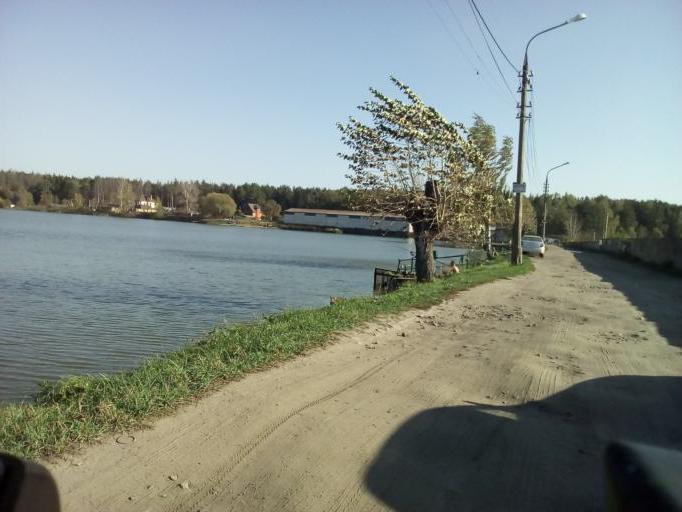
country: RU
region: Moskovskaya
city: Malyshevo
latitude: 55.5561
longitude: 38.3223
